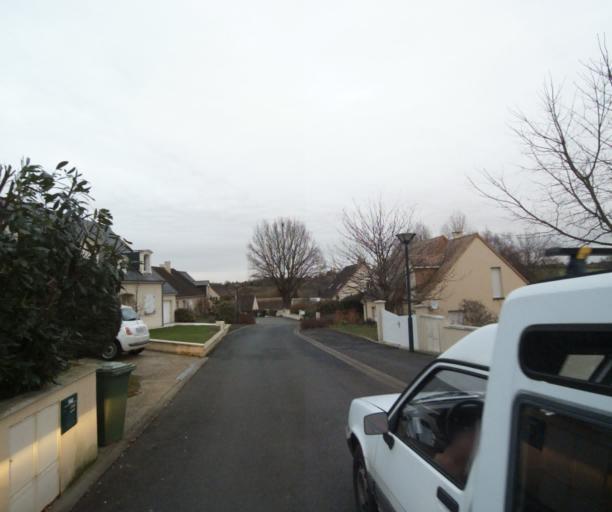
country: FR
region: Pays de la Loire
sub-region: Departement de la Sarthe
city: Coulaines
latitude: 48.0236
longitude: 0.2148
